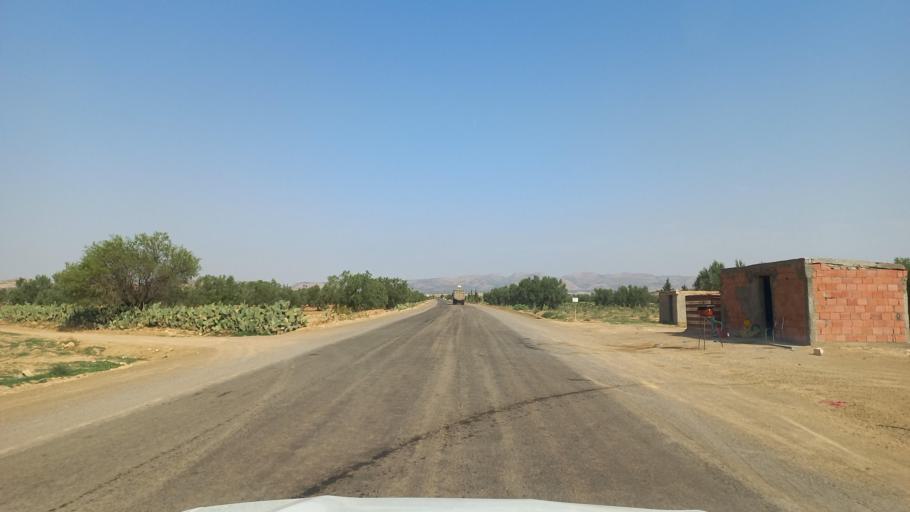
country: TN
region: Al Qasrayn
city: Sbiba
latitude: 35.3472
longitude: 9.0537
